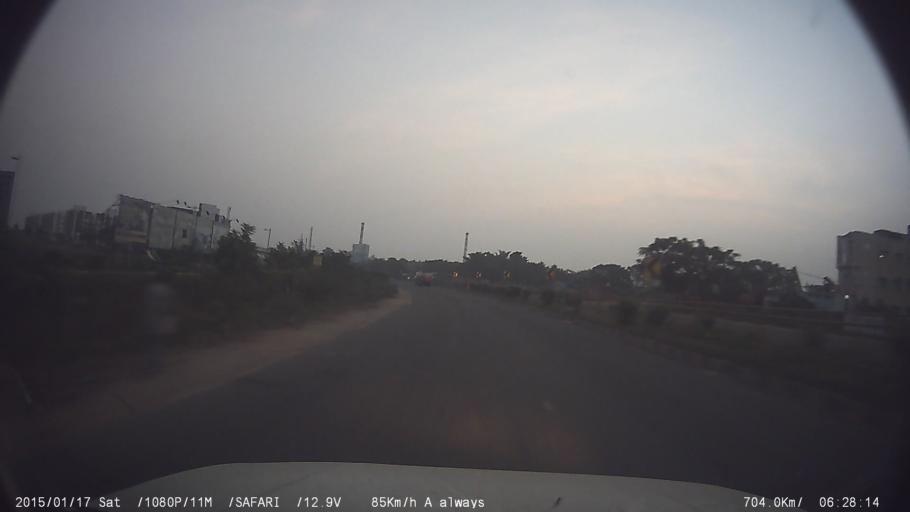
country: IN
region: Tamil Nadu
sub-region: Kancheepuram
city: Sriperumbudur
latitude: 12.9332
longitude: 79.9070
